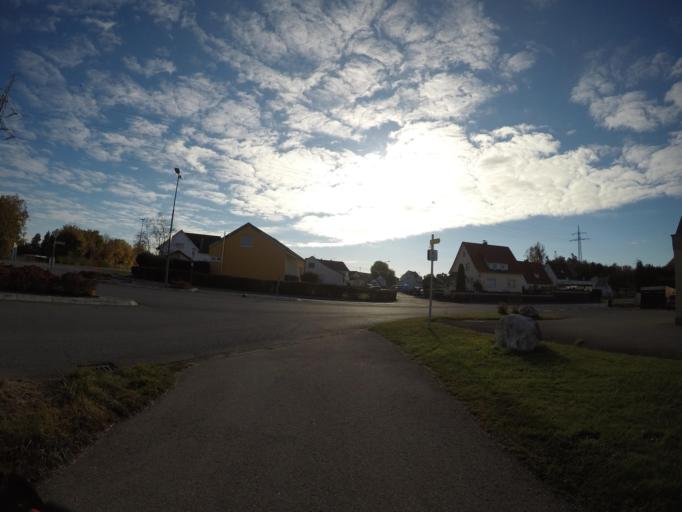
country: DE
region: Baden-Wuerttemberg
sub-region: Tuebingen Region
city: Herbertingen
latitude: 48.0632
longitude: 9.4270
